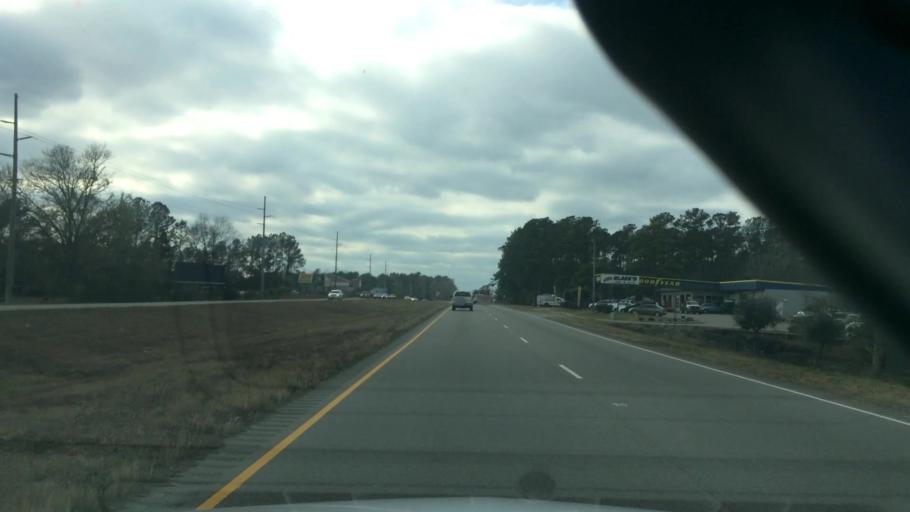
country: US
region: North Carolina
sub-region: Brunswick County
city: Shallotte
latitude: 33.9886
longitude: -78.3555
